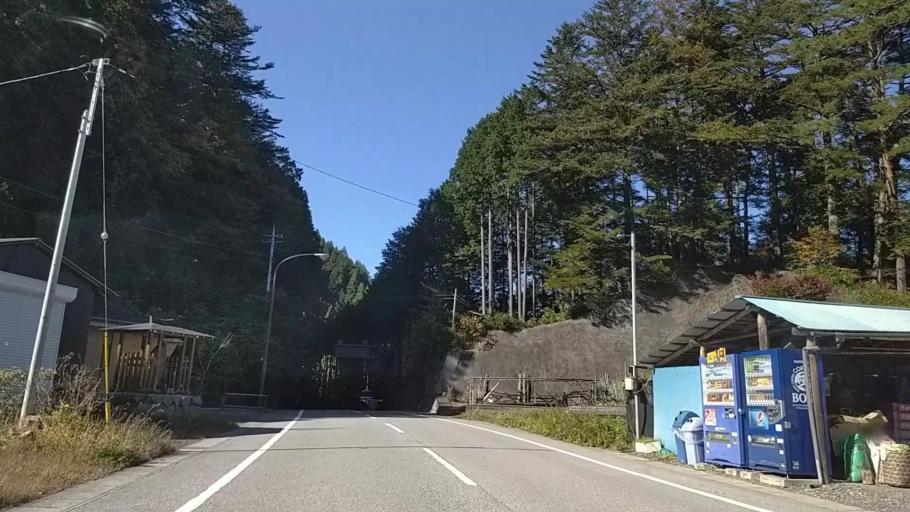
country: JP
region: Yamanashi
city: Otsuki
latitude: 35.7471
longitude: 138.9578
